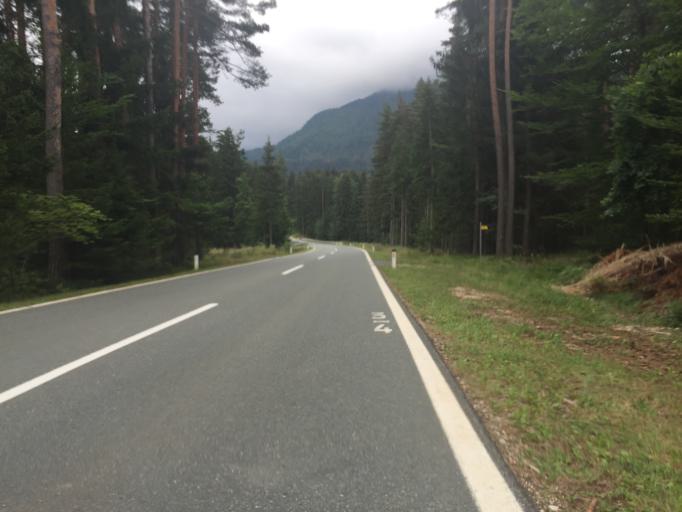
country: AT
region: Carinthia
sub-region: Politischer Bezirk Volkermarkt
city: Feistritz ob Bleiburg
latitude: 46.5489
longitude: 14.7708
